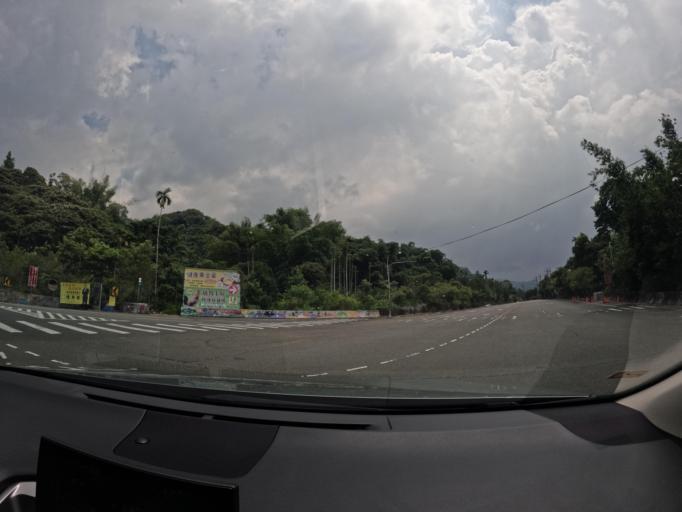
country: TW
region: Taiwan
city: Lugu
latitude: 23.7997
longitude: 120.7891
